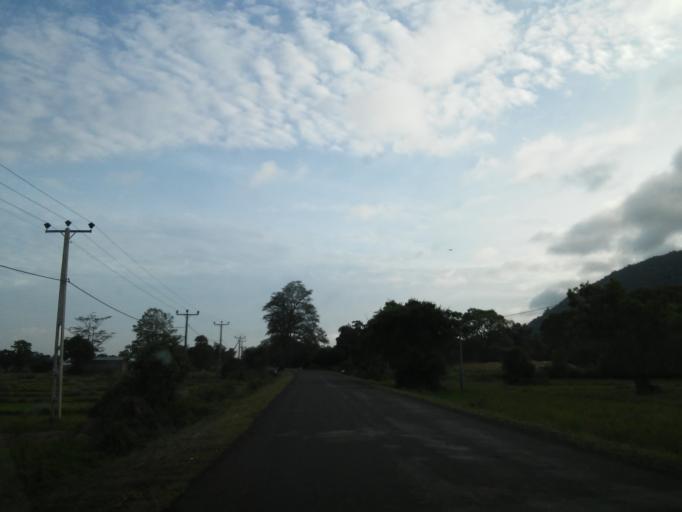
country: LK
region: Central
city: Sigiriya
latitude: 8.1000
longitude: 80.6323
